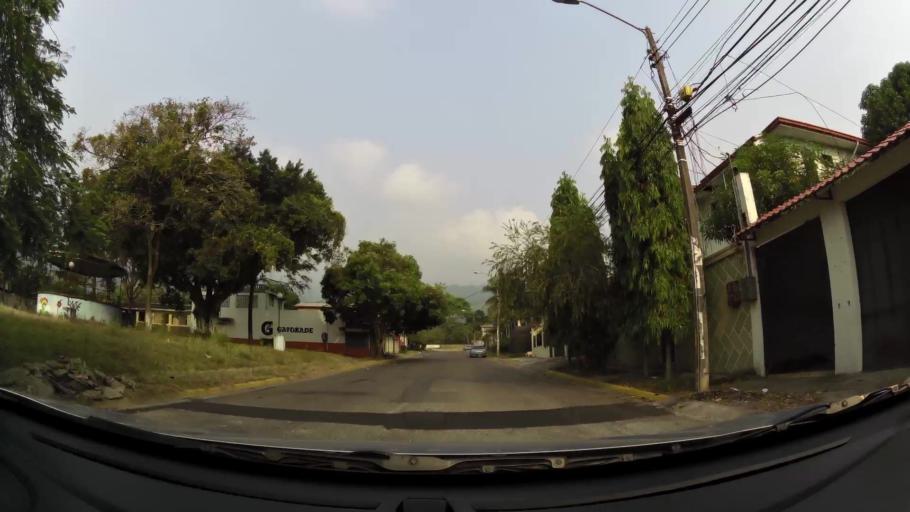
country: HN
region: Cortes
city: Armenta
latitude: 15.4870
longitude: -88.0372
